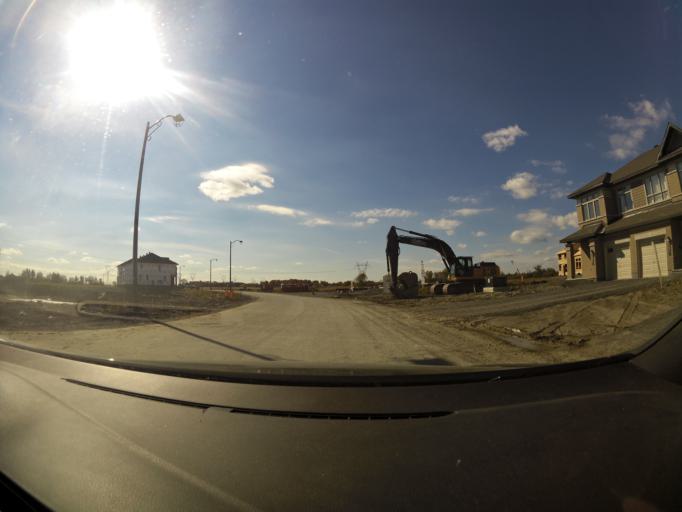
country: CA
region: Ontario
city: Bells Corners
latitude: 45.2801
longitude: -75.8936
